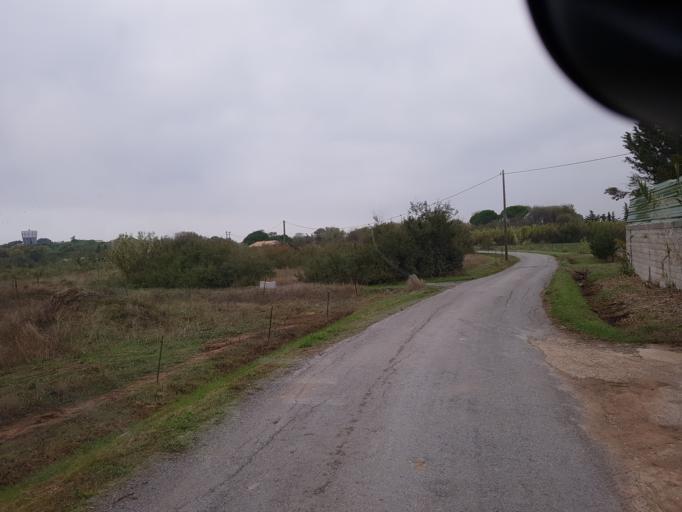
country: FR
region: Languedoc-Roussillon
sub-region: Departement de l'Herault
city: Marseillan
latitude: 43.3676
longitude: 3.5344
